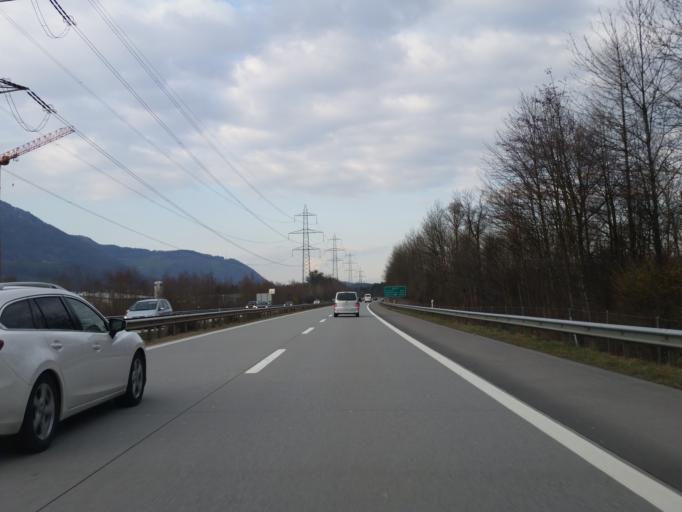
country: LI
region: Ruggell
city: Ruggell
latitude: 47.2508
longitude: 9.5213
